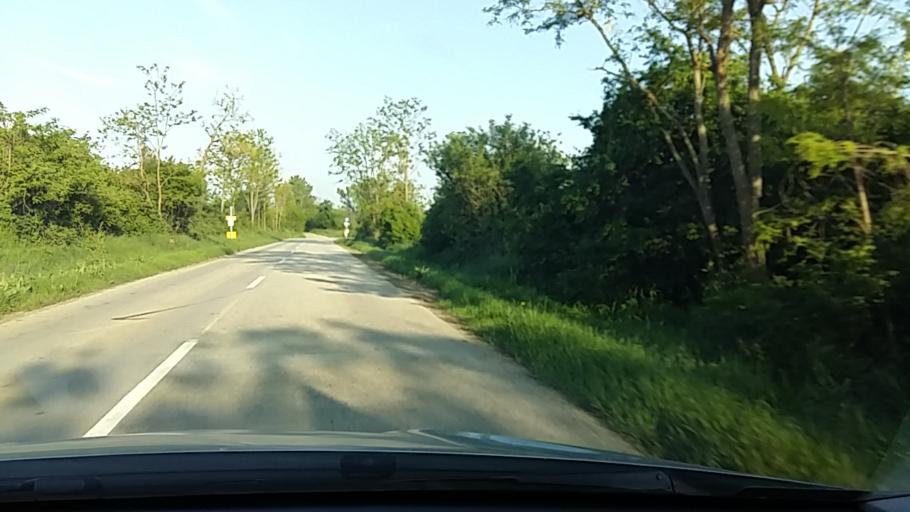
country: HU
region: Pest
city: Szod
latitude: 47.7596
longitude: 19.1872
